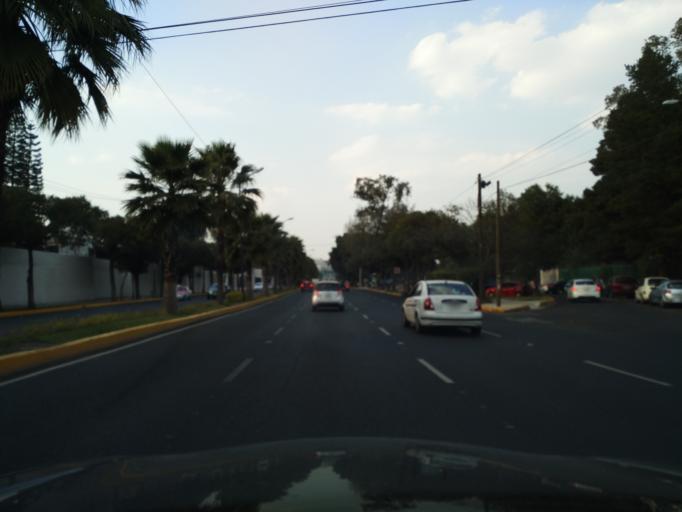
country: MX
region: Mexico City
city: Coyoacan
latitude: 19.3186
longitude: -99.1245
